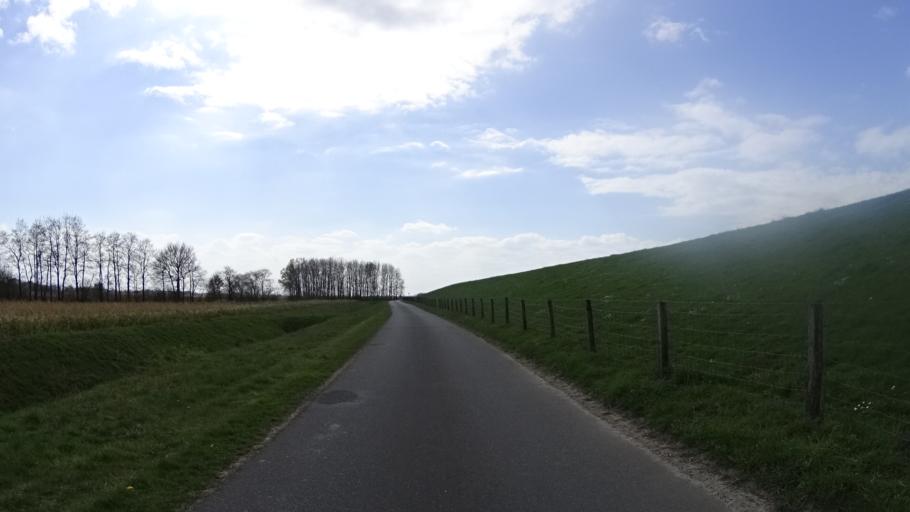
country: DE
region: Lower Saxony
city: Rhede
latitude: 53.1017
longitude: 7.3133
